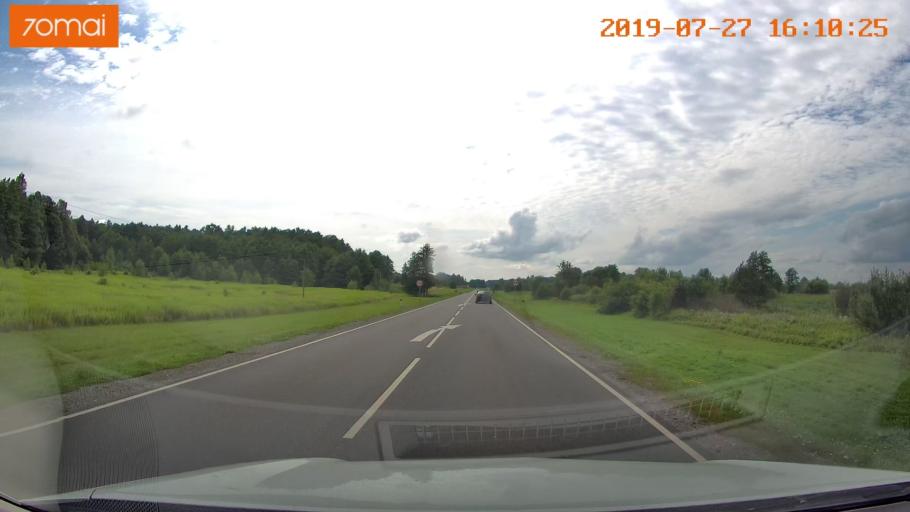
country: RU
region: Kaliningrad
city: Chernyakhovsk
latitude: 54.6361
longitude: 21.6966
